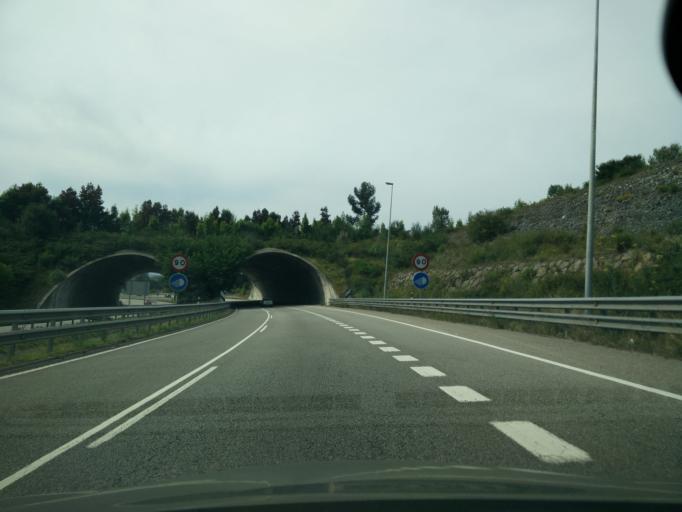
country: ES
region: Asturias
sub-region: Province of Asturias
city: Arriba
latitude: 43.5092
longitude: -5.5961
